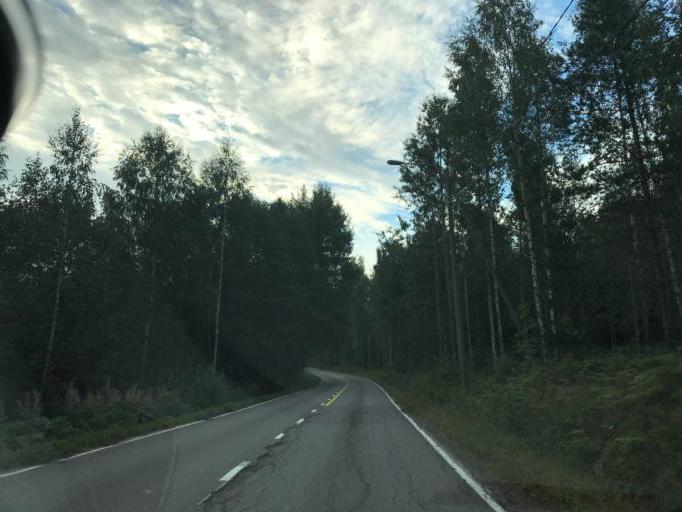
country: FI
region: Uusimaa
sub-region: Helsinki
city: Vihti
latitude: 60.4092
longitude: 24.4794
